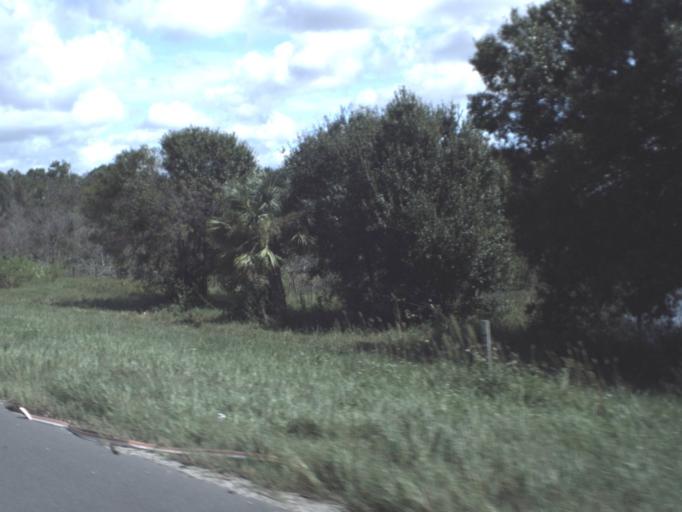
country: US
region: Florida
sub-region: Sarasota County
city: The Meadows
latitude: 27.3682
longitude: -82.4458
